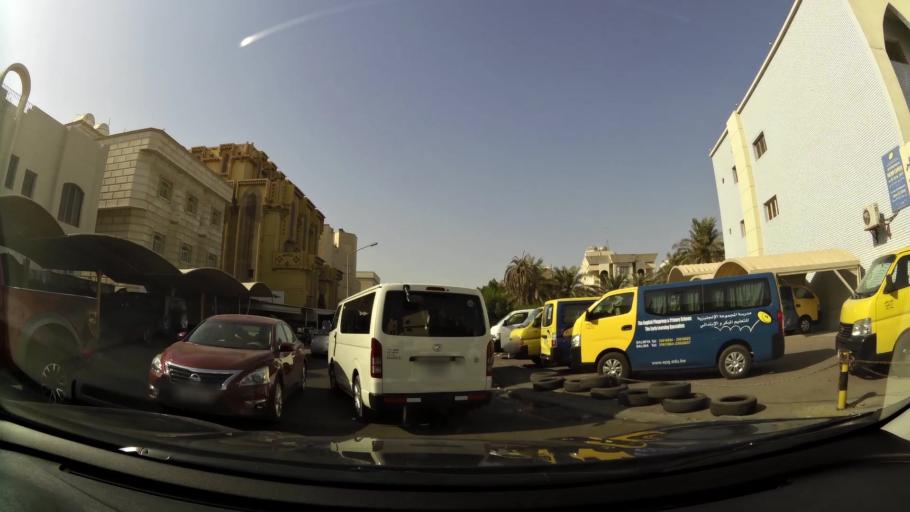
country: KW
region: Muhafazat Hawalli
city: Salwa
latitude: 29.2933
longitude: 48.0714
